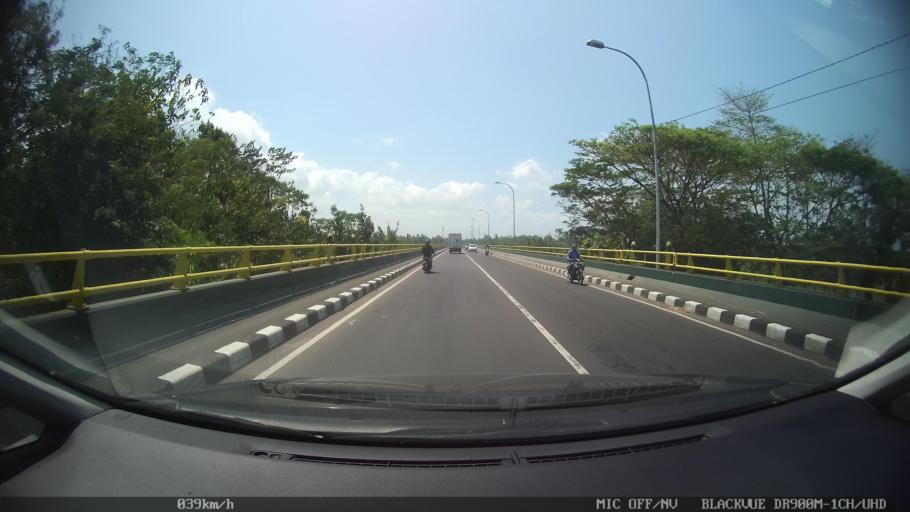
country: ID
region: Daerah Istimewa Yogyakarta
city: Srandakan
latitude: -7.9395
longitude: 110.2393
